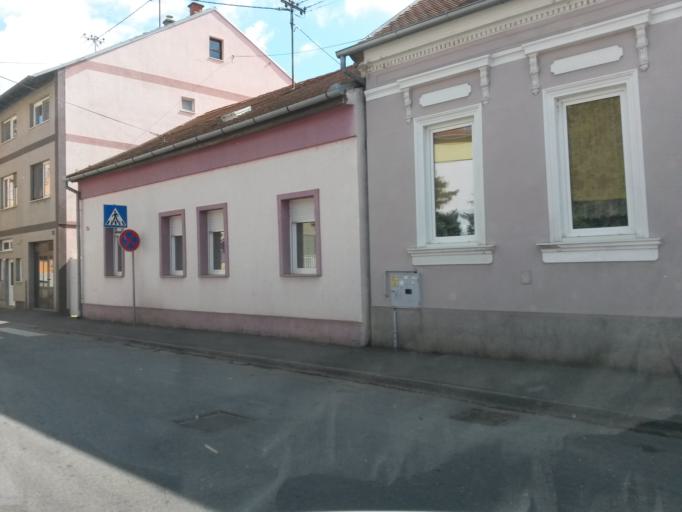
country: HR
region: Osjecko-Baranjska
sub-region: Grad Osijek
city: Osijek
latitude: 45.5603
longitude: 18.6731
